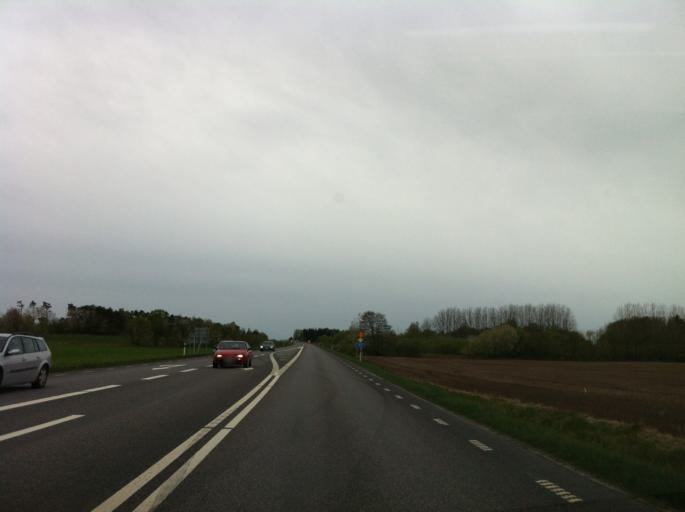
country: SE
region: Halland
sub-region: Falkenbergs Kommun
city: Falkenberg
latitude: 56.9517
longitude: 12.5359
